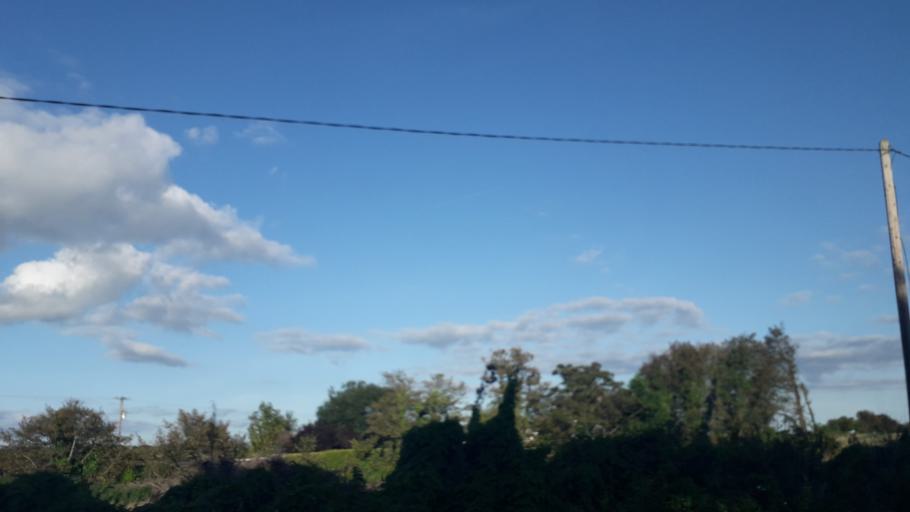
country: IE
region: Leinster
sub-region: Lu
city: Carlingford
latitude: 54.0248
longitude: -6.1496
